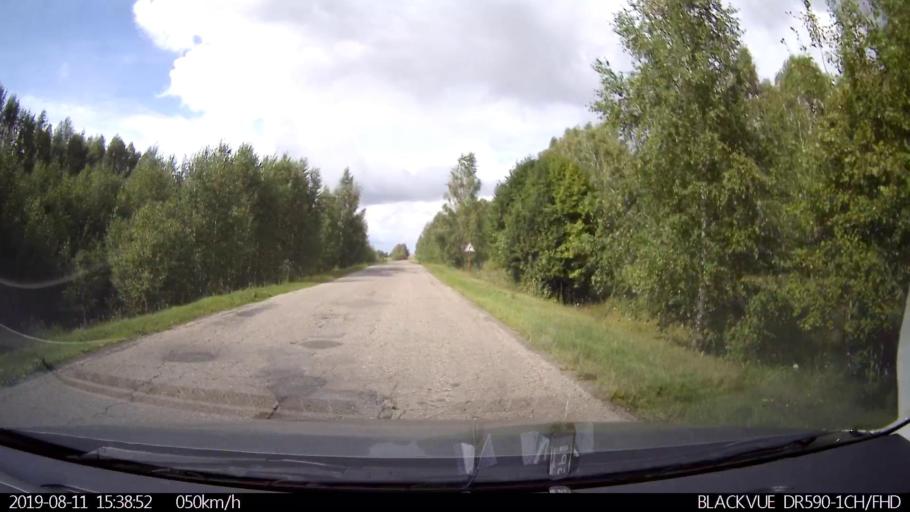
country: RU
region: Ulyanovsk
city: Ignatovka
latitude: 53.8644
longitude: 47.6399
